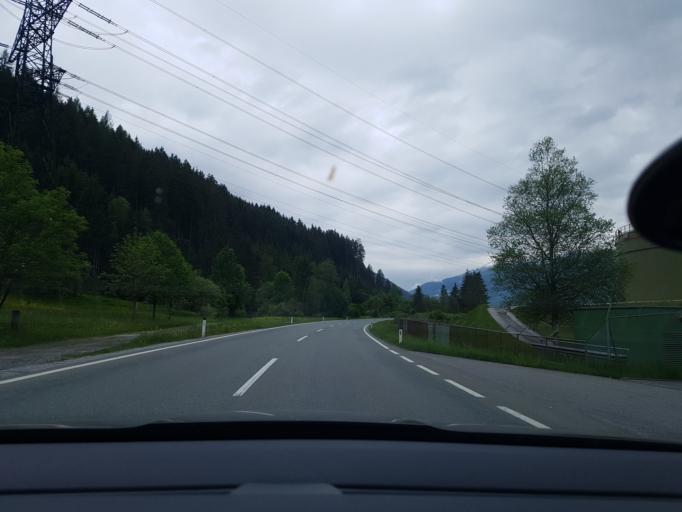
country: AT
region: Salzburg
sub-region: Politischer Bezirk Zell am See
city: Hollersbach im Pinzgau
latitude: 47.2759
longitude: 12.4437
